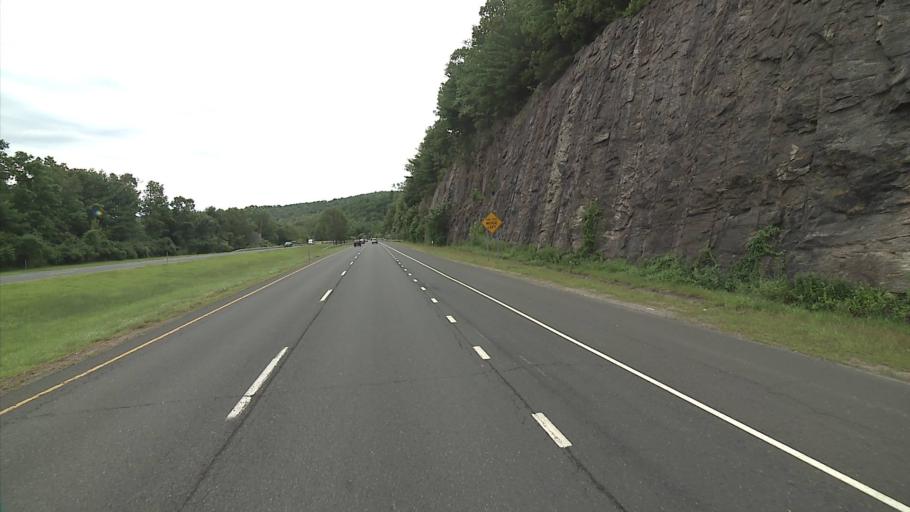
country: US
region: Connecticut
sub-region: Litchfield County
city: Thomaston
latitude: 41.6511
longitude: -73.0801
